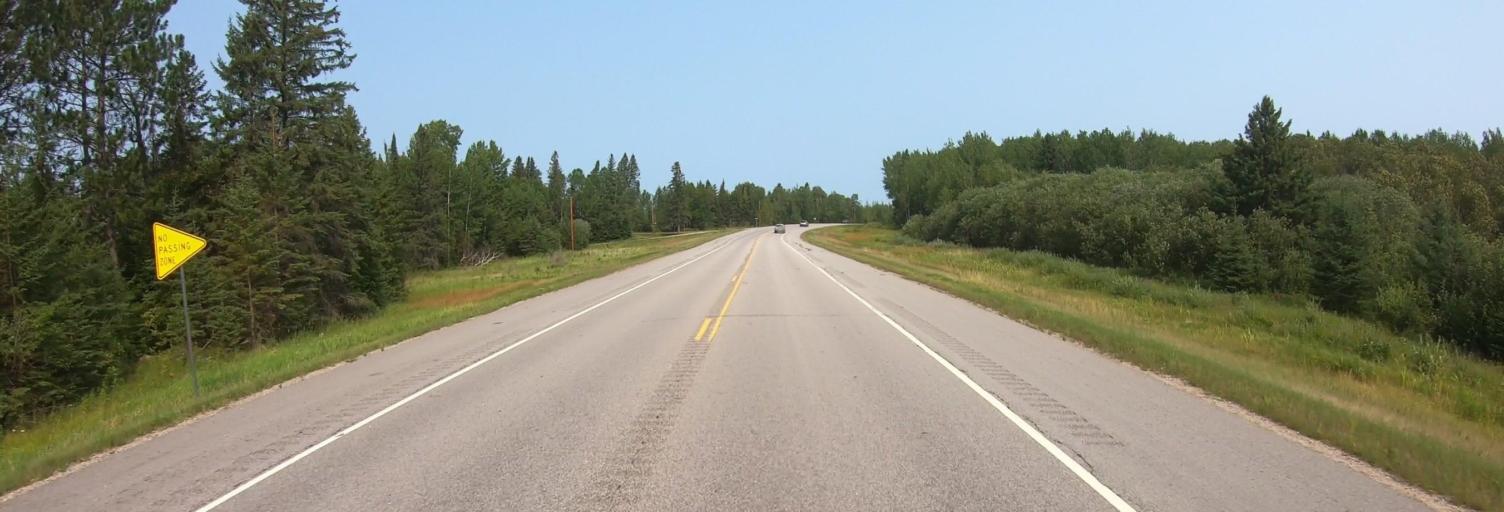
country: CA
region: Ontario
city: Fort Frances
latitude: 48.2957
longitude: -92.9704
